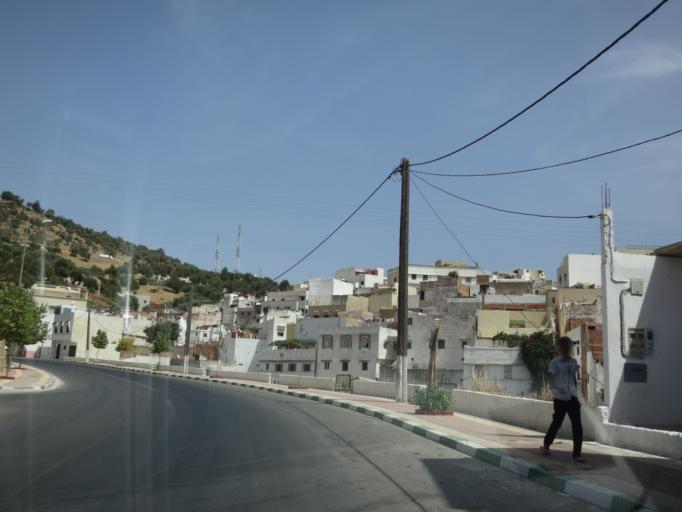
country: MA
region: Meknes-Tafilalet
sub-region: Meknes
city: Meknes
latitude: 34.0574
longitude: -5.5261
